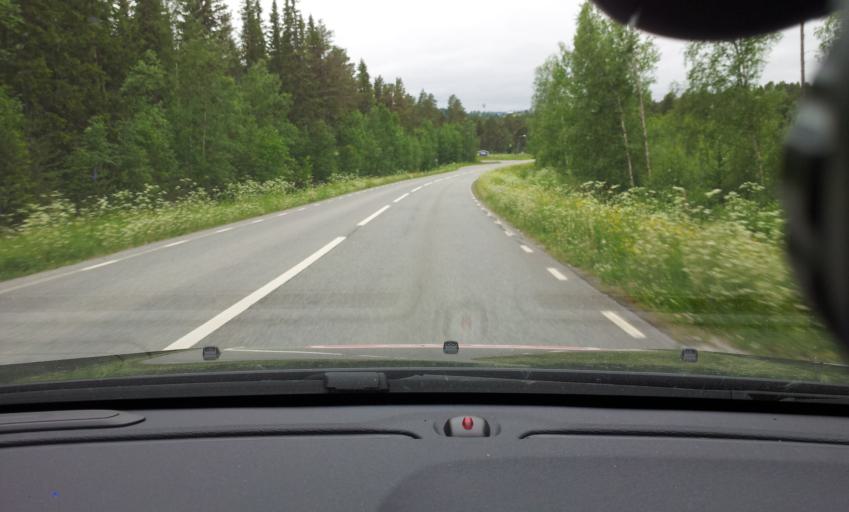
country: SE
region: Jaemtland
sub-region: Bergs Kommun
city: Hoverberg
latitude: 63.0003
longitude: 14.3644
